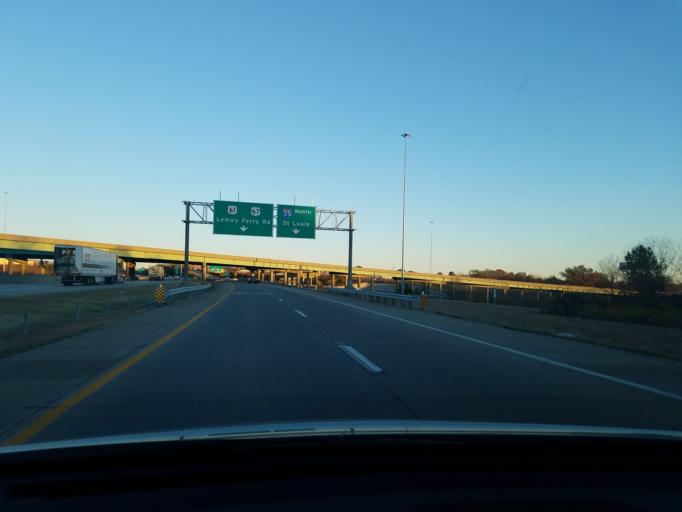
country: US
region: Missouri
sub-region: Saint Louis County
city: Mehlville
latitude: 38.5038
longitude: -90.3411
